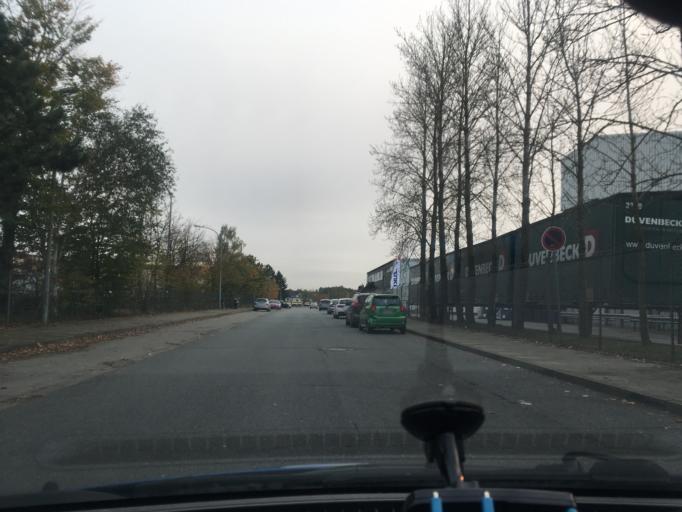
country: DE
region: Lower Saxony
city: Adendorf
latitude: 53.2770
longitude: 10.4225
